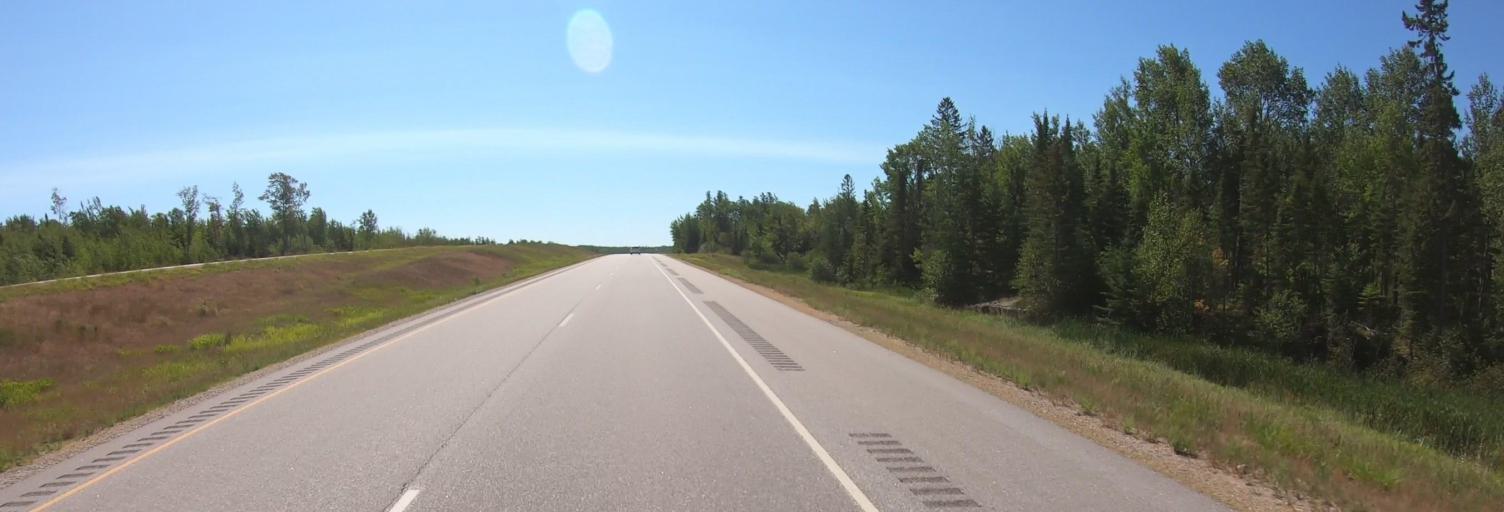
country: US
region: Minnesota
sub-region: Saint Louis County
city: Mountain Iron
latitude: 47.7510
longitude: -92.6510
